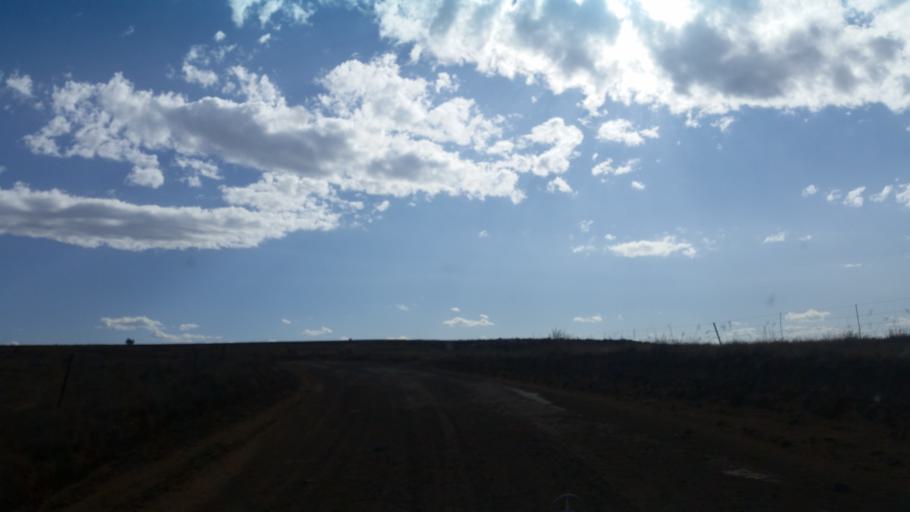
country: ZA
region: Orange Free State
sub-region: Thabo Mofutsanyana District Municipality
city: Phuthaditjhaba
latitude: -28.3506
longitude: 28.6066
